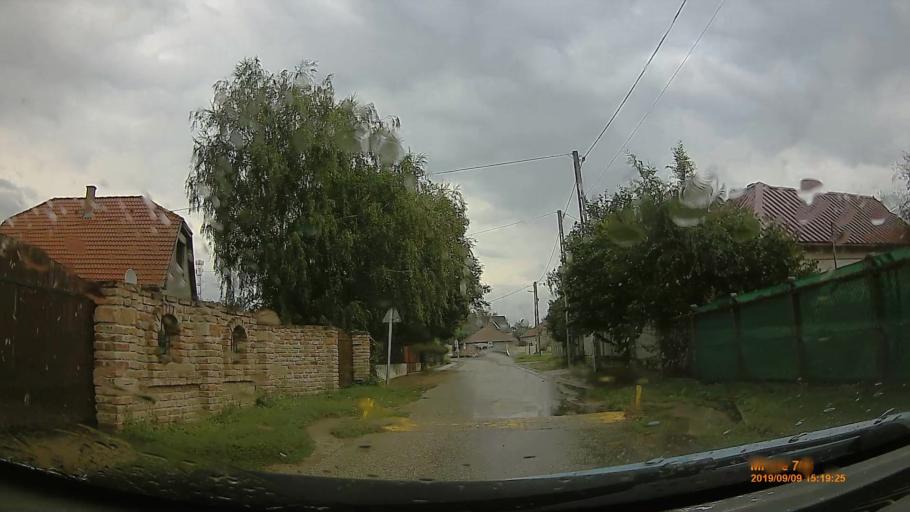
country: HU
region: Szabolcs-Szatmar-Bereg
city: Nyirpazony
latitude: 48.0140
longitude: 21.8309
